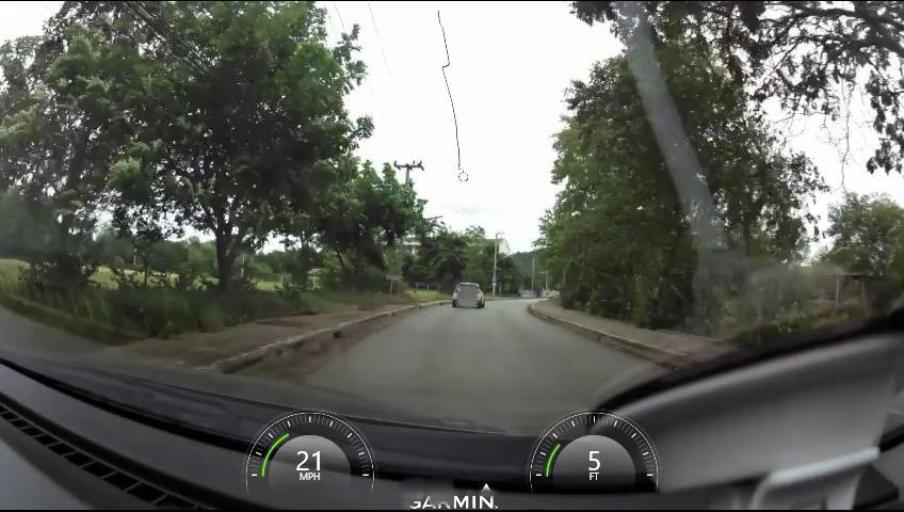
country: TH
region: Prachuap Khiri Khan
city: Pran Buri
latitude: 12.4606
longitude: 99.9753
